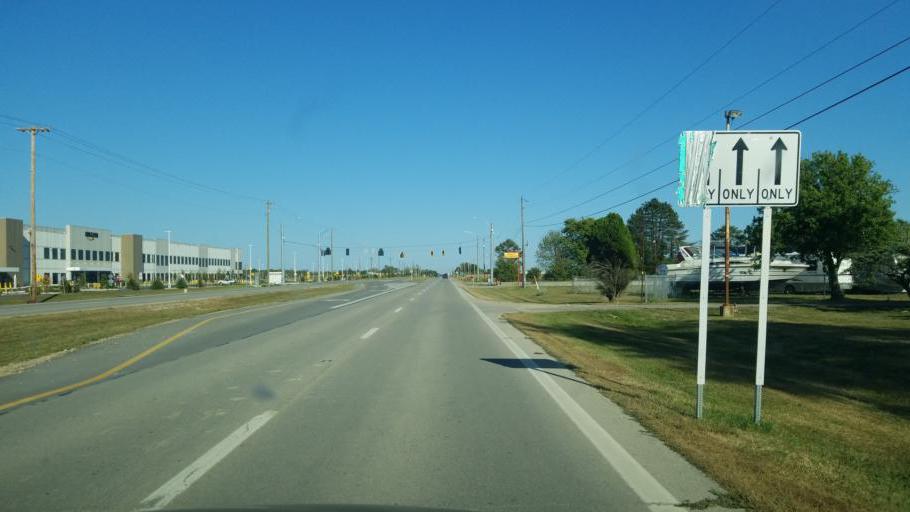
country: US
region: Ohio
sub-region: Madison County
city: West Jefferson
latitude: 39.9419
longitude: -83.3206
